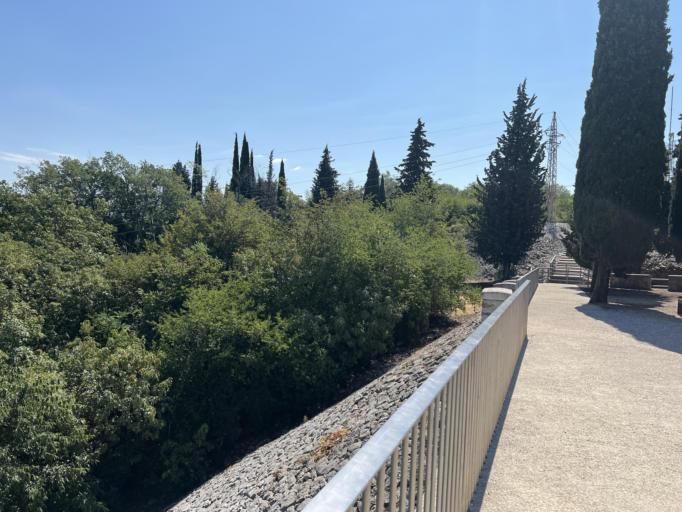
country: IT
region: Friuli Venezia Giulia
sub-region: Provincia di Gorizia
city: Farra d'Isonzo
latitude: 45.8862
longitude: 13.5416
